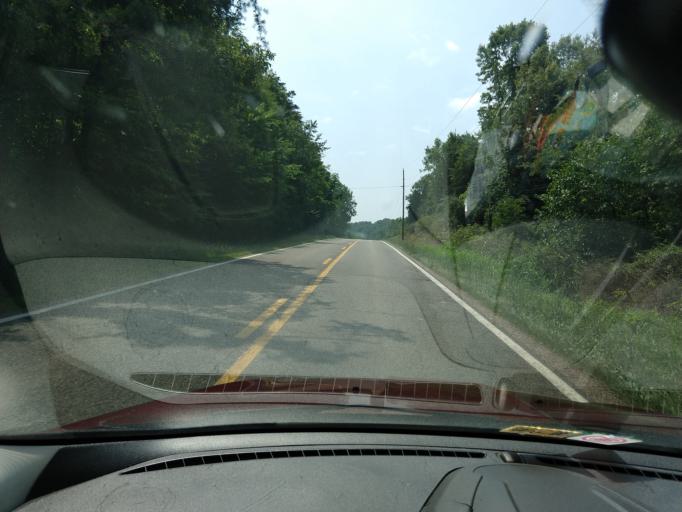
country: US
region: West Virginia
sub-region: Jackson County
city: Ripley
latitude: 38.8478
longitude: -81.7988
